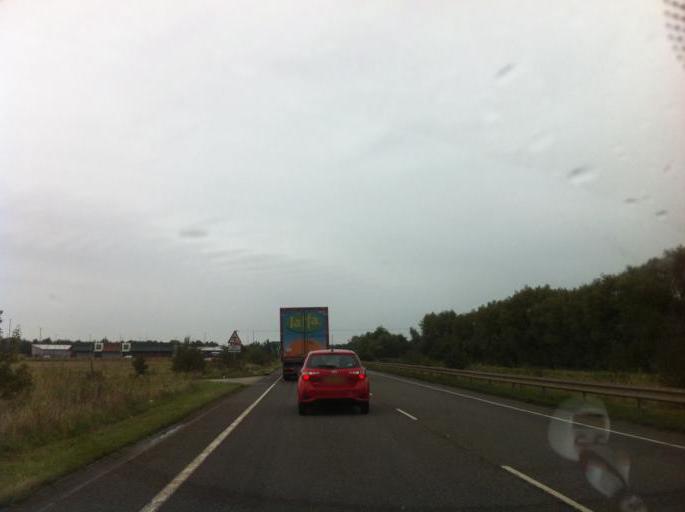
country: GB
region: England
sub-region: Lincolnshire
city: Kirton
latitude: 52.8864
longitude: -0.0866
